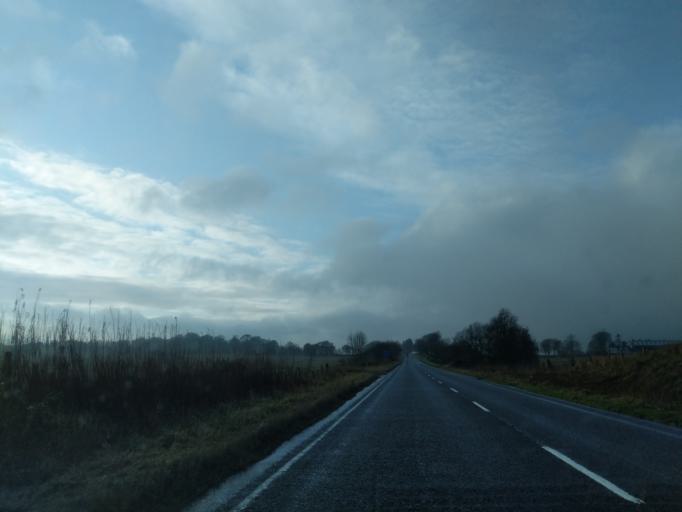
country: GB
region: Scotland
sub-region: Perth and Kinross
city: Kinross
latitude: 56.1987
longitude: -3.5080
